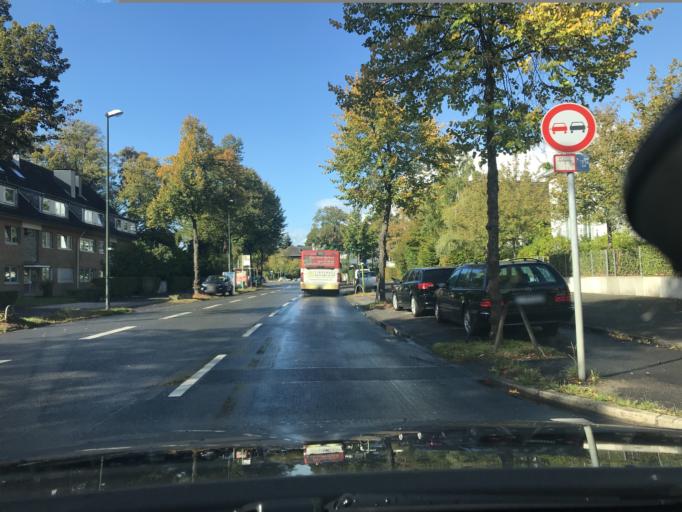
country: DE
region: North Rhine-Westphalia
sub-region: Regierungsbezirk Dusseldorf
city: Dusseldorf
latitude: 51.2671
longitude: 6.7501
